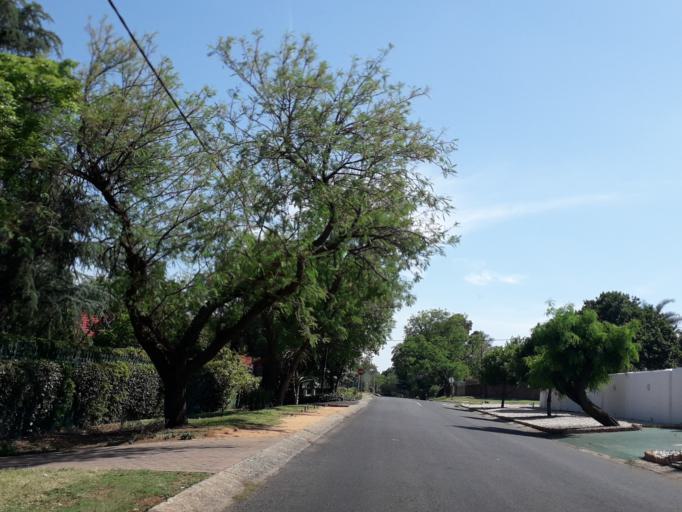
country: ZA
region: Gauteng
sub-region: City of Johannesburg Metropolitan Municipality
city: Johannesburg
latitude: -26.1177
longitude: 27.9978
